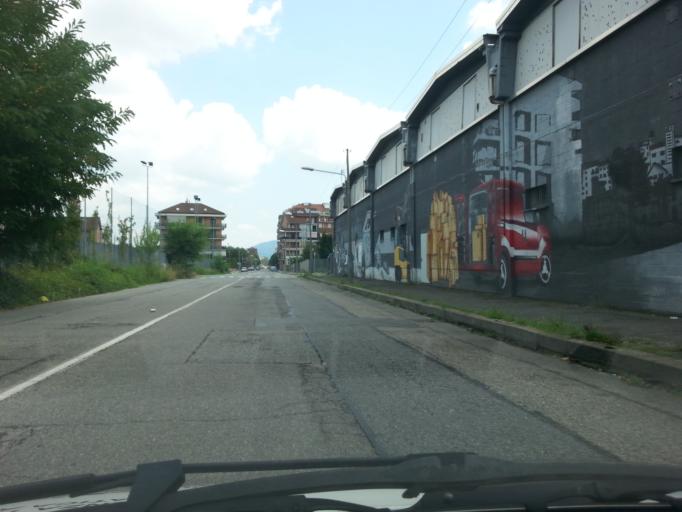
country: IT
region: Piedmont
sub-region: Provincia di Torino
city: Turin
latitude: 45.1075
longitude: 7.6746
